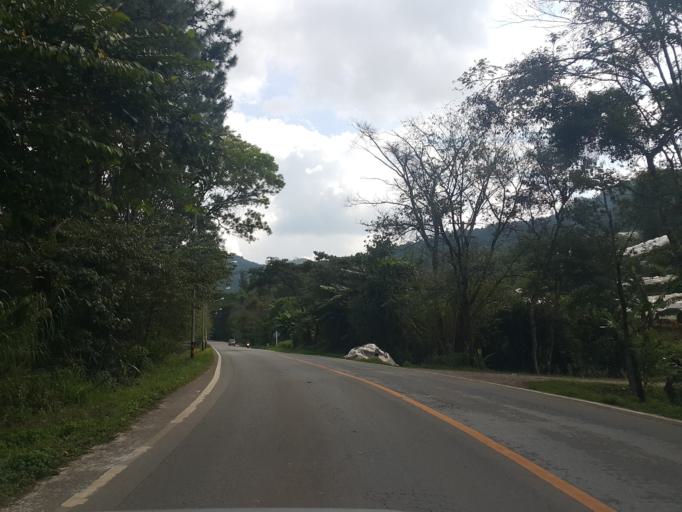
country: TH
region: Chiang Mai
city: Mae Chaem
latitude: 18.5344
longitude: 98.5218
